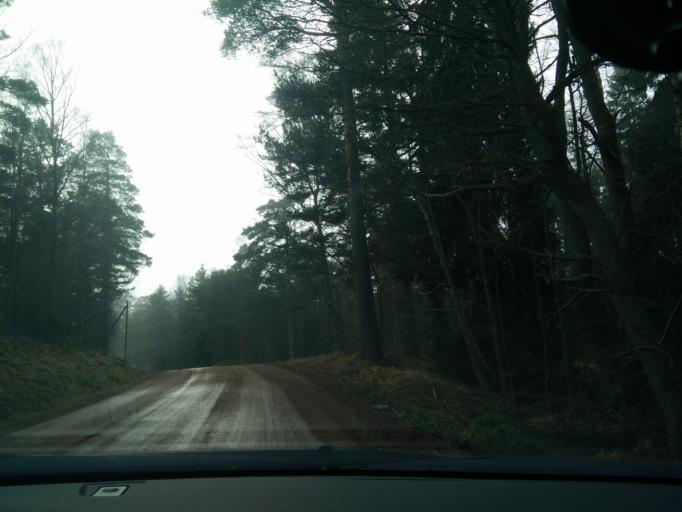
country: AX
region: Mariehamns stad
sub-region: Mariehamn
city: Mariehamn
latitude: 60.0936
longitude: 19.9129
